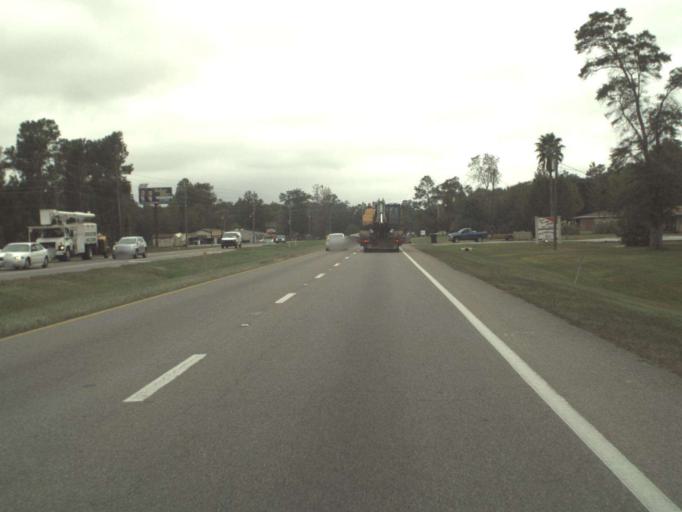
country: US
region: Florida
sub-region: Escambia County
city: Gonzalez
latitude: 30.5901
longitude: -87.3075
